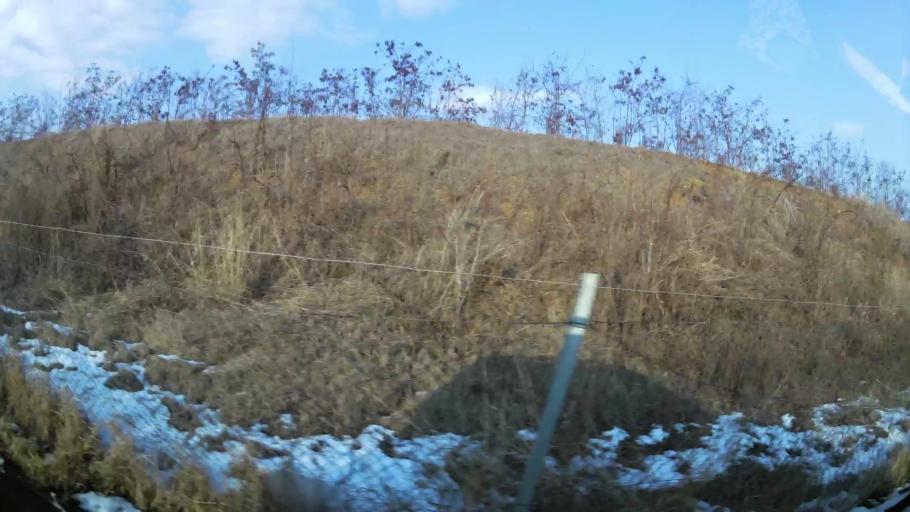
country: MK
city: Creshevo
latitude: 42.0327
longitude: 21.5247
